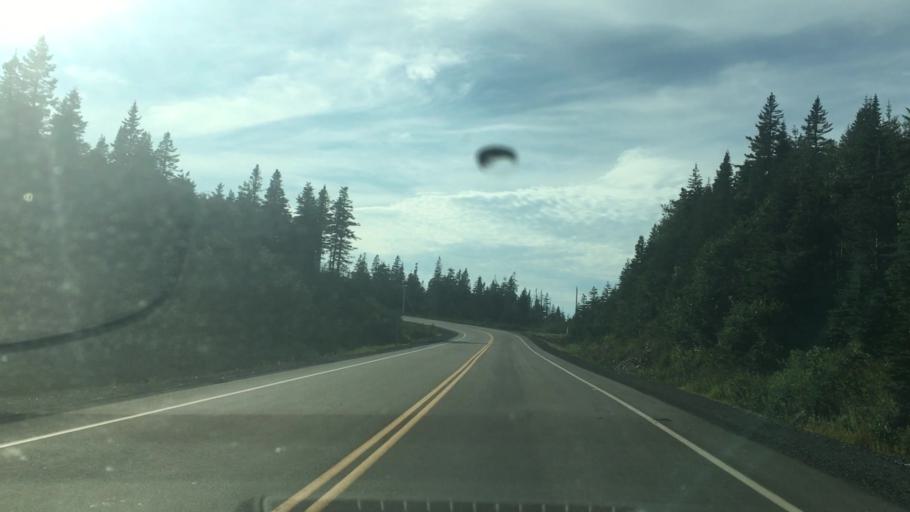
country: CA
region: Nova Scotia
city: Sydney Mines
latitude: 46.8239
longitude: -60.6567
